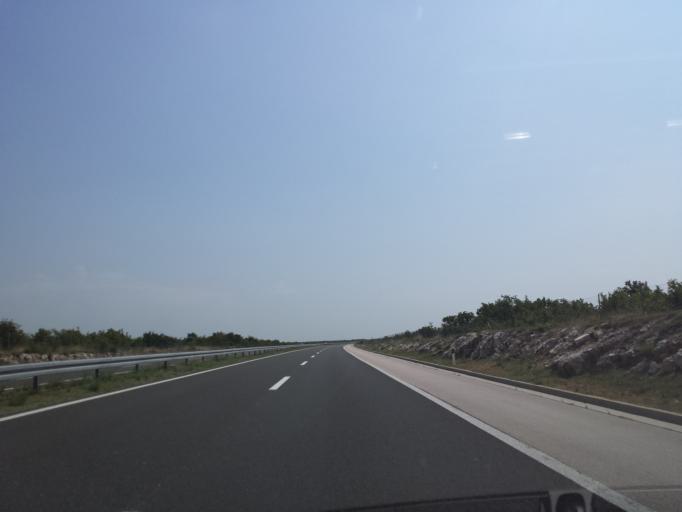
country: HR
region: Zadarska
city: Polaca
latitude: 44.0860
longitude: 15.5003
